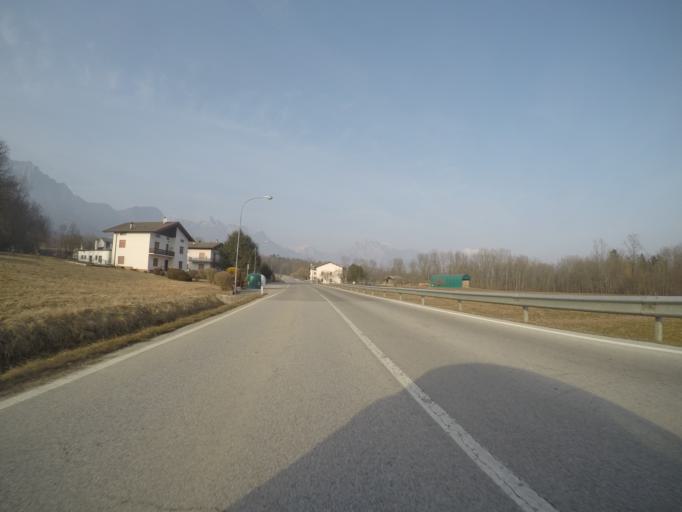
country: IT
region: Veneto
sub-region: Provincia di Belluno
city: Sedico
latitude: 46.1149
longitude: 12.0749
